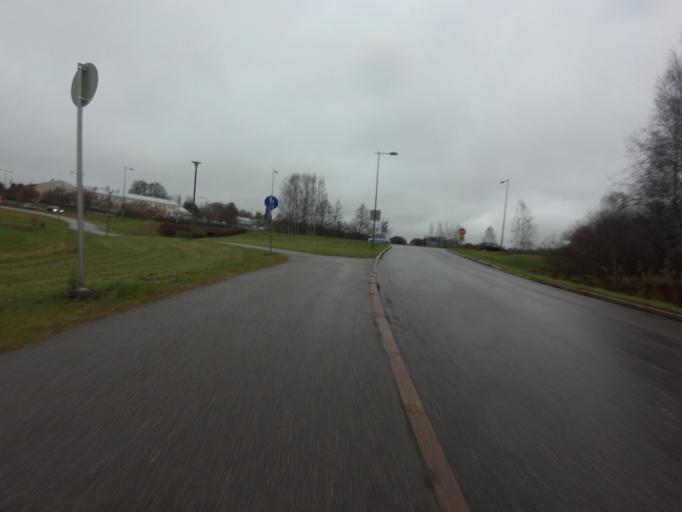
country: FI
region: Uusimaa
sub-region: Helsinki
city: Espoo
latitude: 60.2109
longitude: 24.6555
